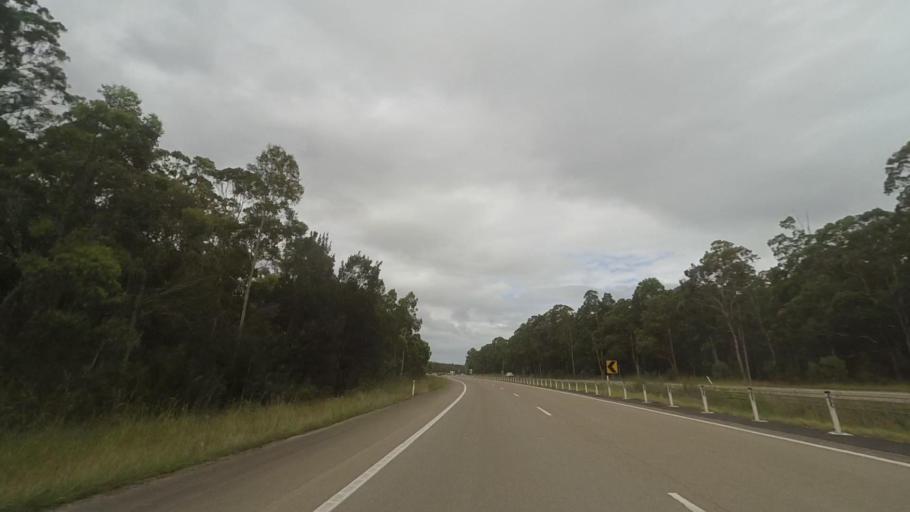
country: AU
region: New South Wales
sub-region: Port Stephens Shire
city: Medowie
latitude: -32.6506
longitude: 151.9086
